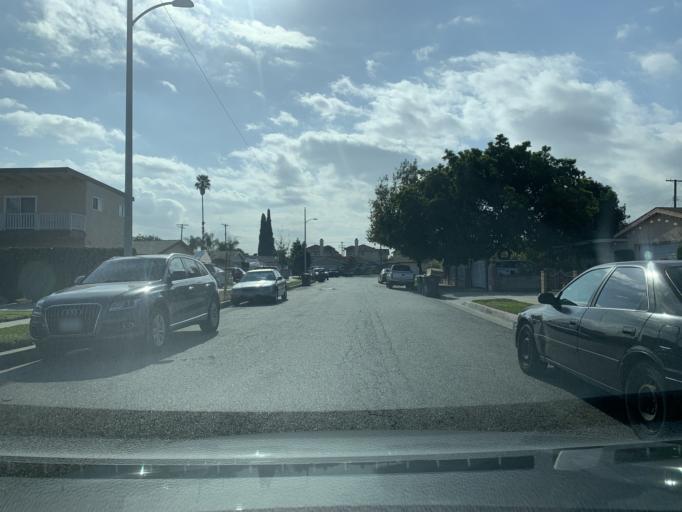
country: US
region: California
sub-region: Los Angeles County
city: Rosemead
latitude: 34.0665
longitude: -118.0601
